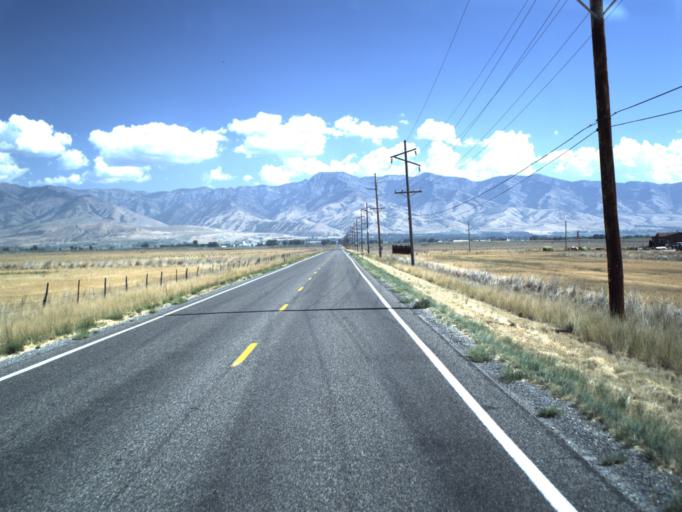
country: US
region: Utah
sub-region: Cache County
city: Benson
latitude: 41.8449
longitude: -111.9455
